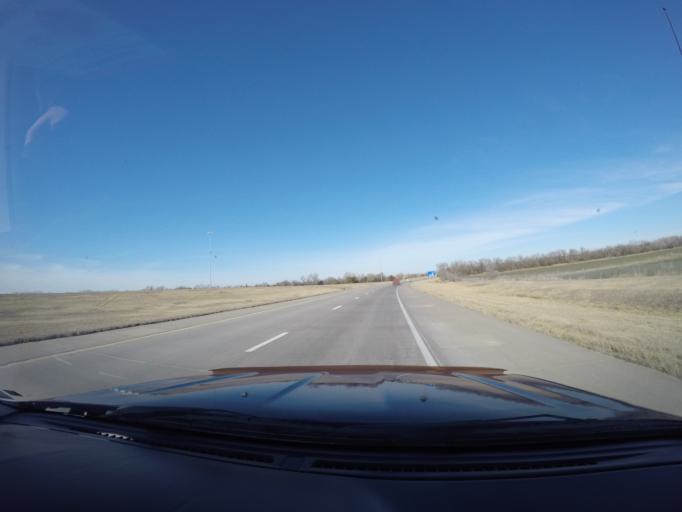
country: US
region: Kansas
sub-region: Harvey County
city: Newton
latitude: 38.0278
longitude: -97.3276
